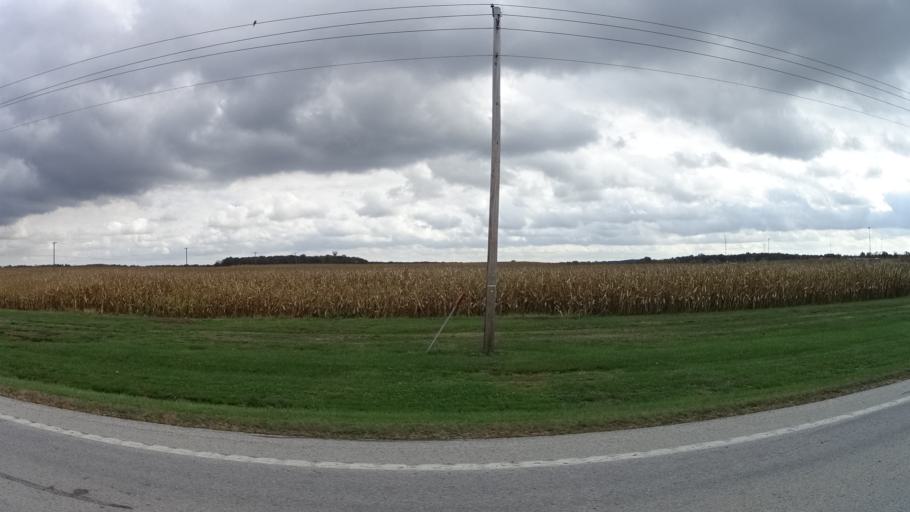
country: US
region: Ohio
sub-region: Lorain County
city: Eaton Estates
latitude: 41.2880
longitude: -82.0210
